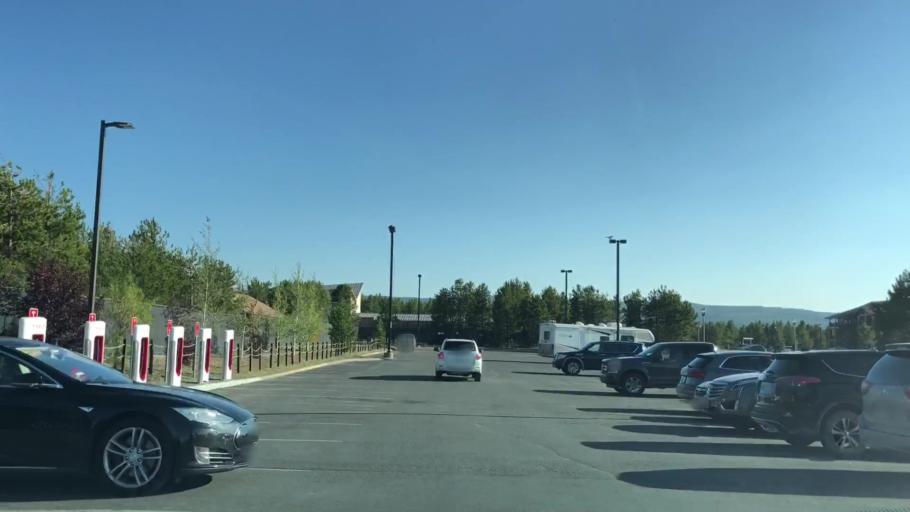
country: US
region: Montana
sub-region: Gallatin County
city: West Yellowstone
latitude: 44.6562
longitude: -111.0991
